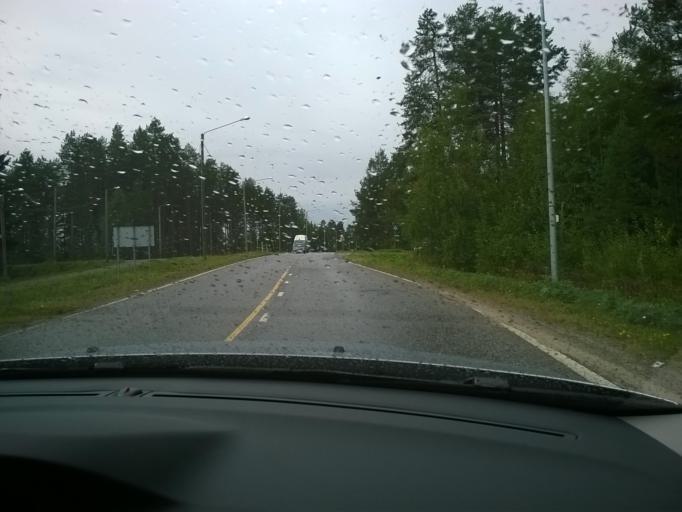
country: FI
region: Kainuu
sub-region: Kehys-Kainuu
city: Kuhmo
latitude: 64.1208
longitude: 29.5470
